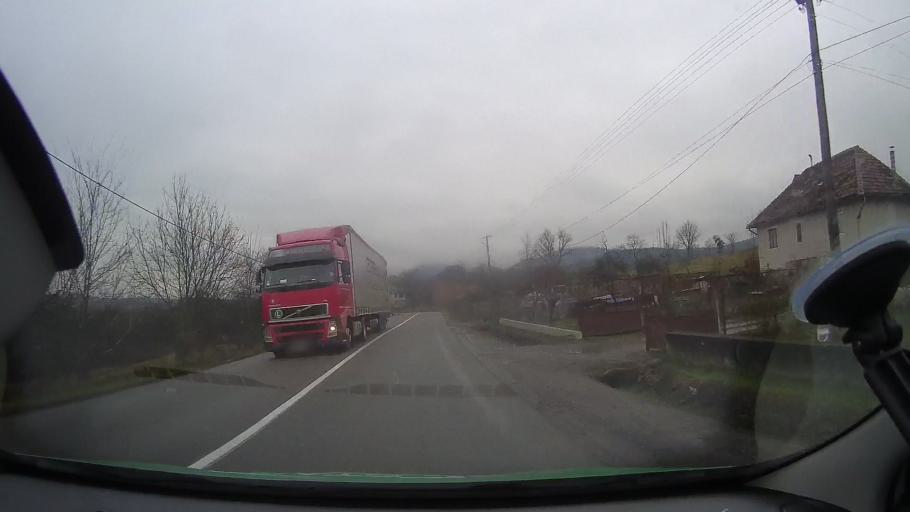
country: RO
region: Arad
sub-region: Comuna Varfurile
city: Varfurile
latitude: 46.3154
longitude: 22.5123
